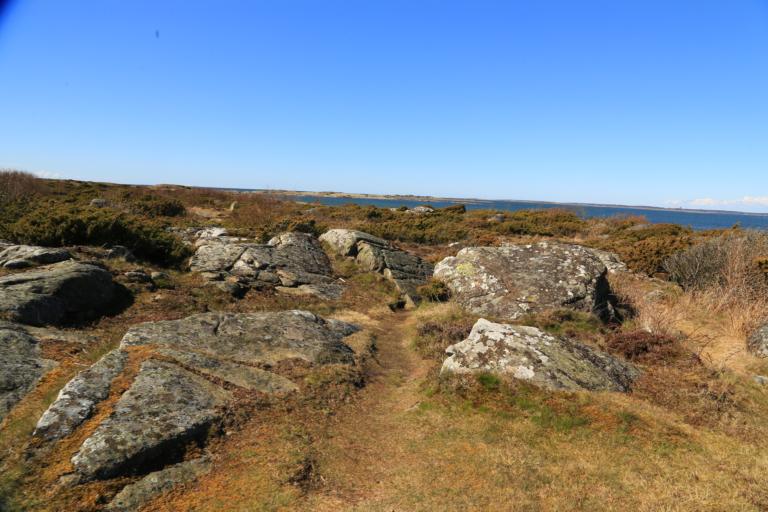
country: SE
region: Halland
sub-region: Varbergs Kommun
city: Varberg
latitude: 57.1210
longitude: 12.1982
